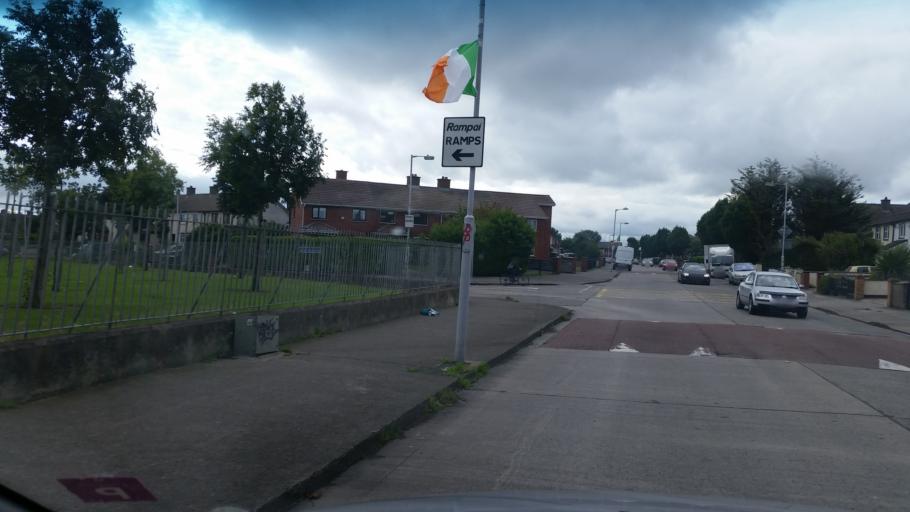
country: IE
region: Leinster
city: Raheny
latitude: 53.3935
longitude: -6.1785
